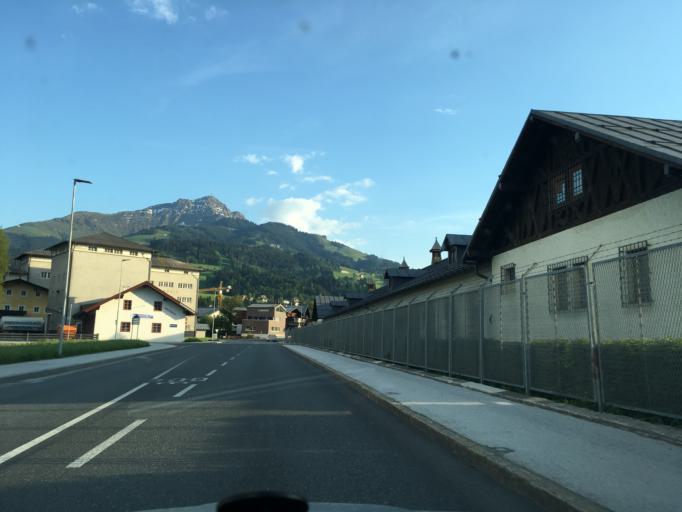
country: AT
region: Tyrol
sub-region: Politischer Bezirk Kitzbuhel
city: Sankt Johann in Tirol
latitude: 47.5259
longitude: 12.4322
